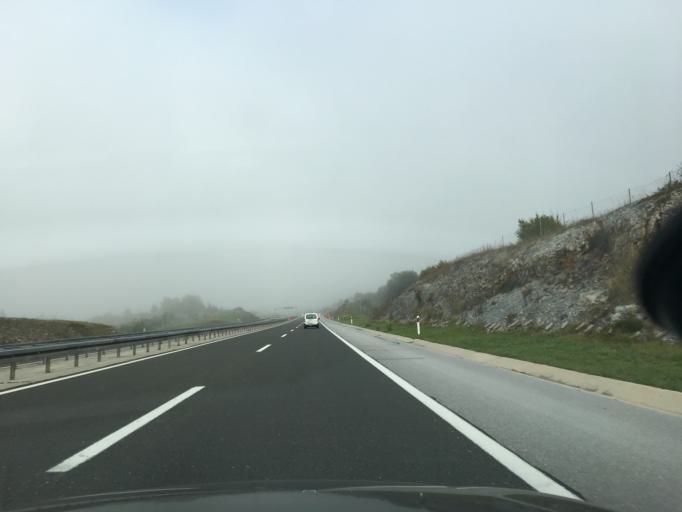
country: HR
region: Licko-Senjska
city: Brinje
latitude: 44.9514
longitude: 15.1399
